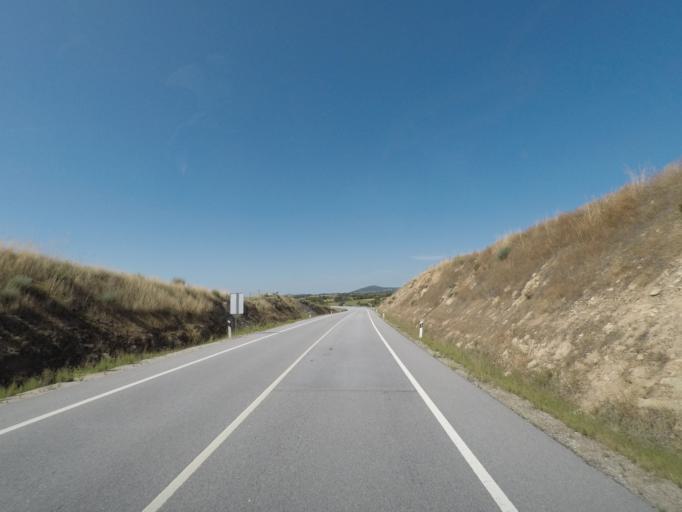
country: ES
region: Castille and Leon
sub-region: Provincia de Salamanca
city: Villarino de los Aires
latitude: 41.3667
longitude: -6.5202
